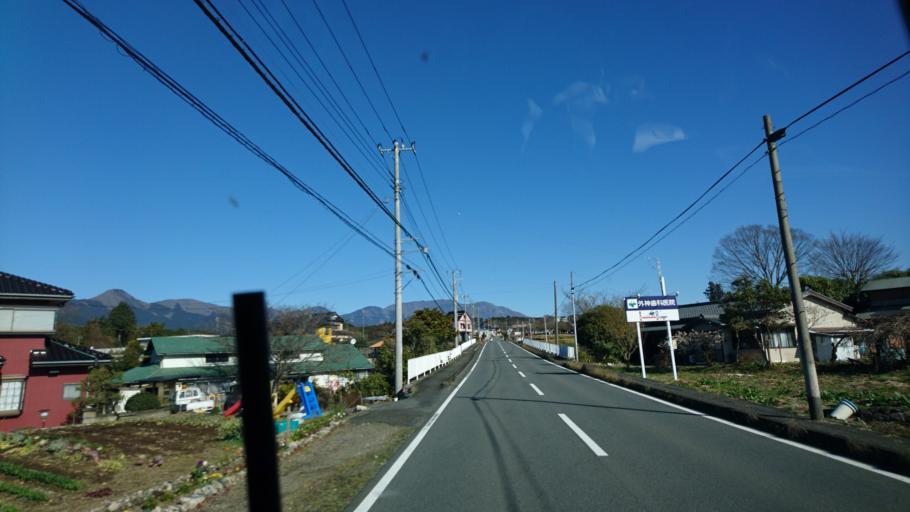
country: JP
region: Shizuoka
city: Fujinomiya
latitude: 35.2816
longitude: 138.6037
